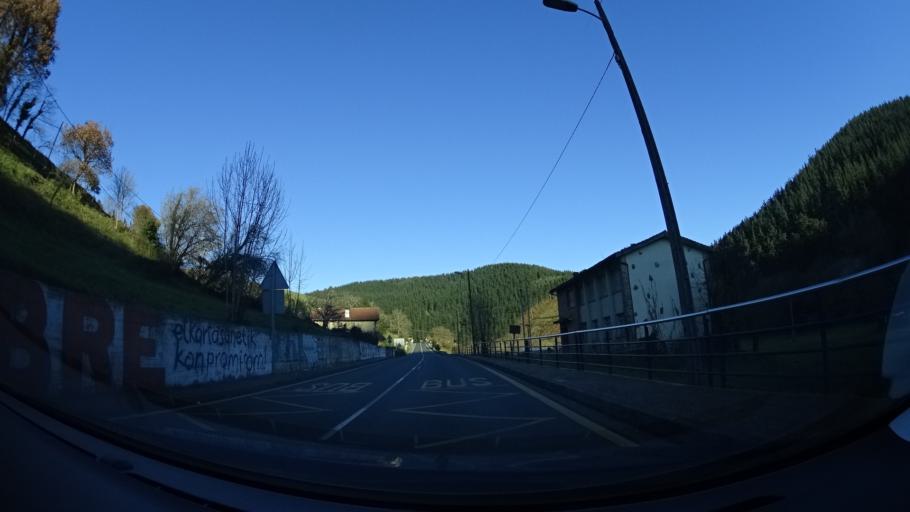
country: ES
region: Basque Country
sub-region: Bizkaia
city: Amoroto
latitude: 43.3436
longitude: -2.5055
